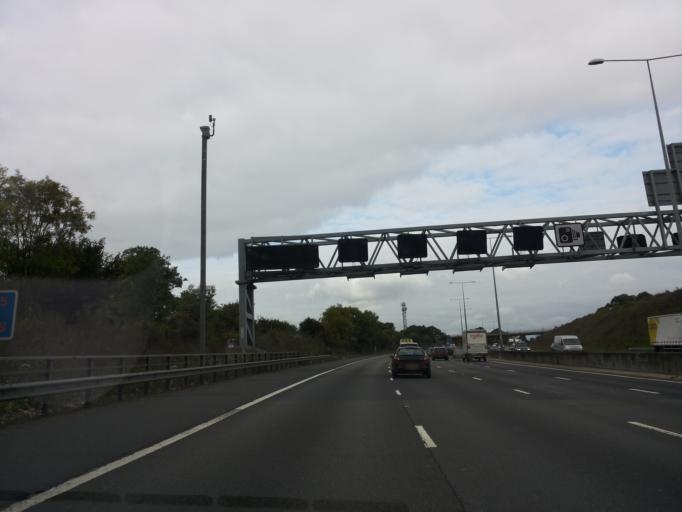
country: GB
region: England
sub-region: Hertfordshire
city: Chorleywood
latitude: 51.6677
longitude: -0.4920
